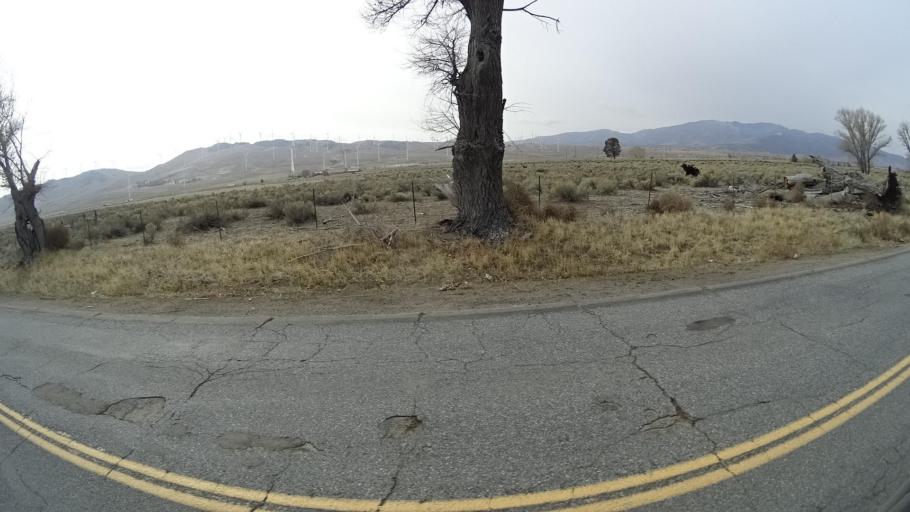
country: US
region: California
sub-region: Kern County
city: Tehachapi
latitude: 35.1214
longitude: -118.3701
